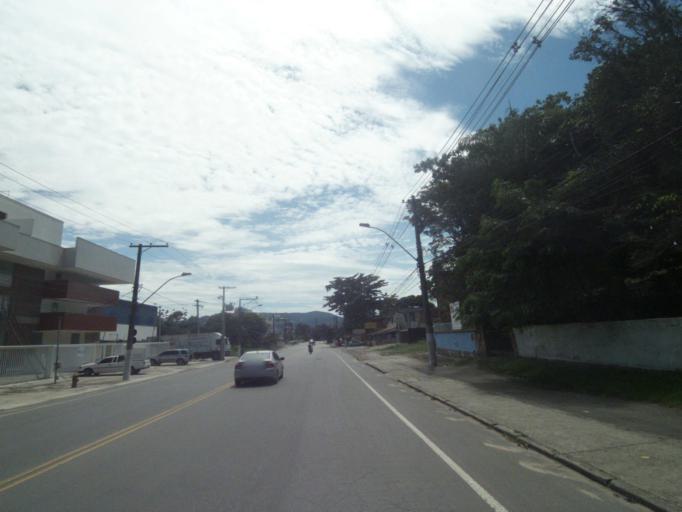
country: BR
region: Rio de Janeiro
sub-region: Niteroi
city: Niteroi
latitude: -22.9619
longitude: -43.0302
